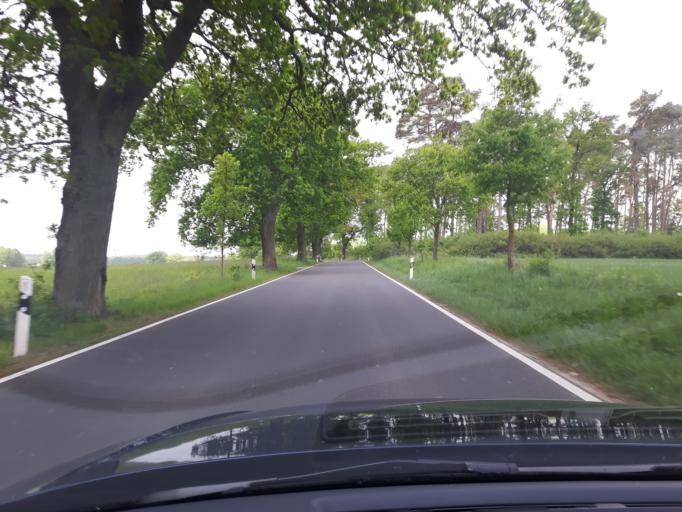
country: DE
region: Mecklenburg-Vorpommern
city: Grabowhofe
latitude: 53.5799
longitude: 12.5206
